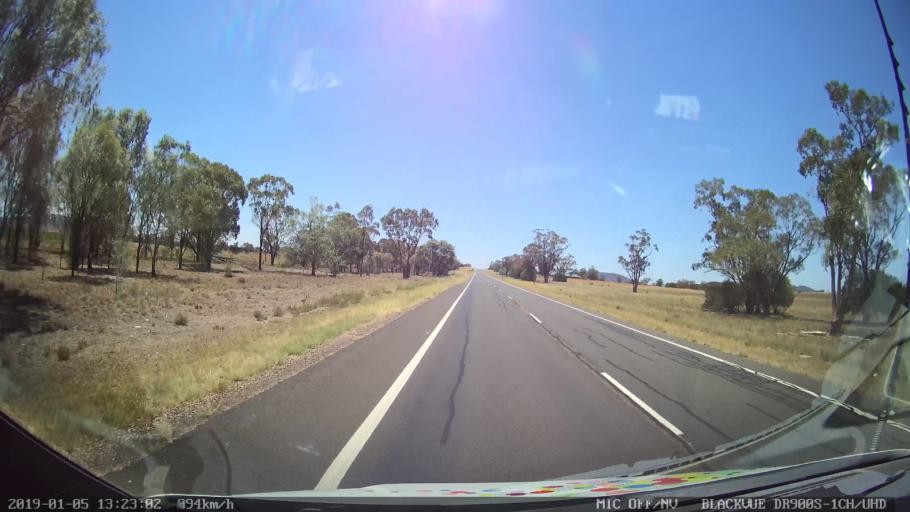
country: AU
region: New South Wales
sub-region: Gunnedah
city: Gunnedah
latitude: -31.0812
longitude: 149.9700
